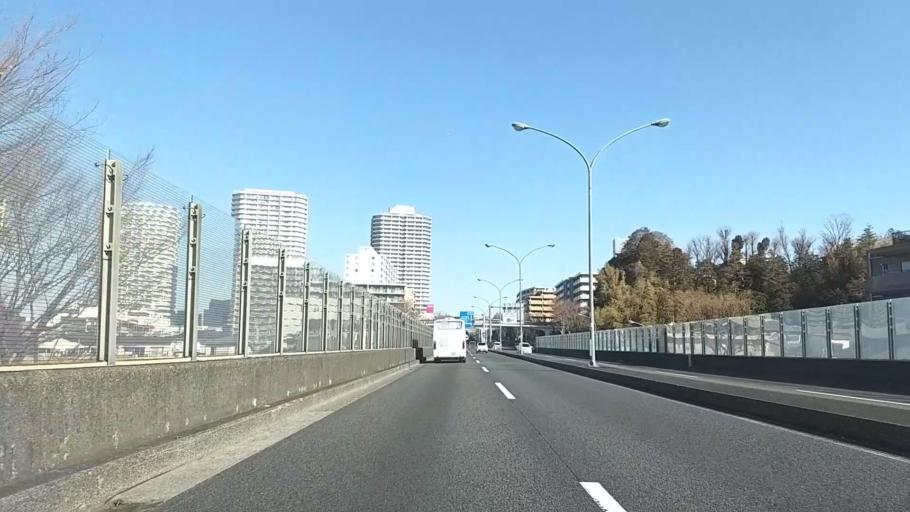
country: JP
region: Kanagawa
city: Yokohama
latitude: 35.4258
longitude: 139.5613
